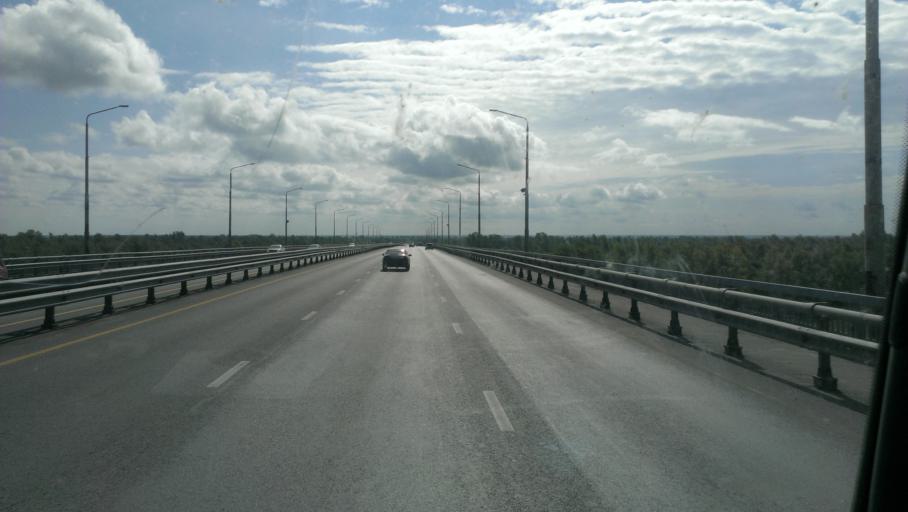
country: RU
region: Altai Krai
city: Zaton
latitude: 53.3230
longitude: 83.8042
